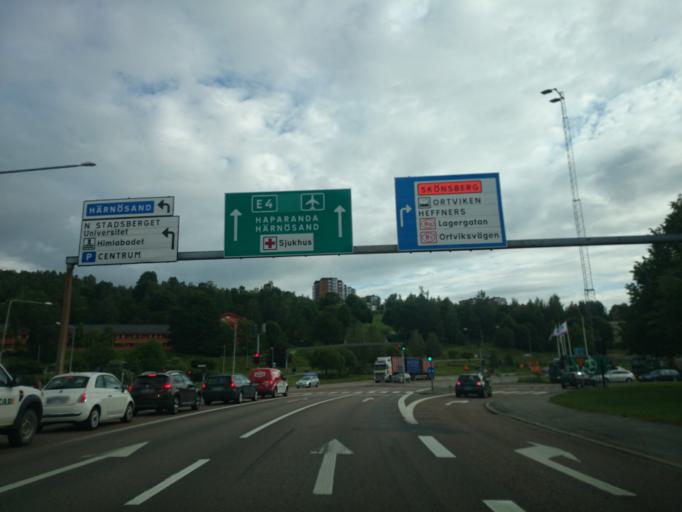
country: SE
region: Vaesternorrland
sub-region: Sundsvalls Kommun
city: Sundsvall
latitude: 62.3936
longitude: 17.3131
